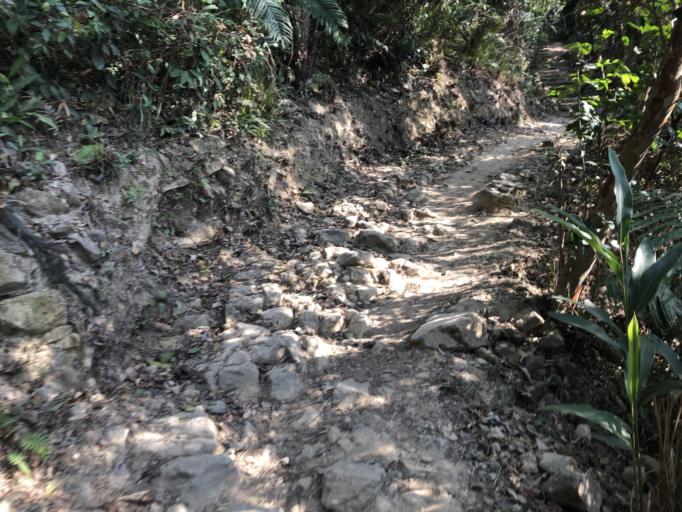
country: HK
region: Sai Kung
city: Sai Kung
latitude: 22.3663
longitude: 114.2904
